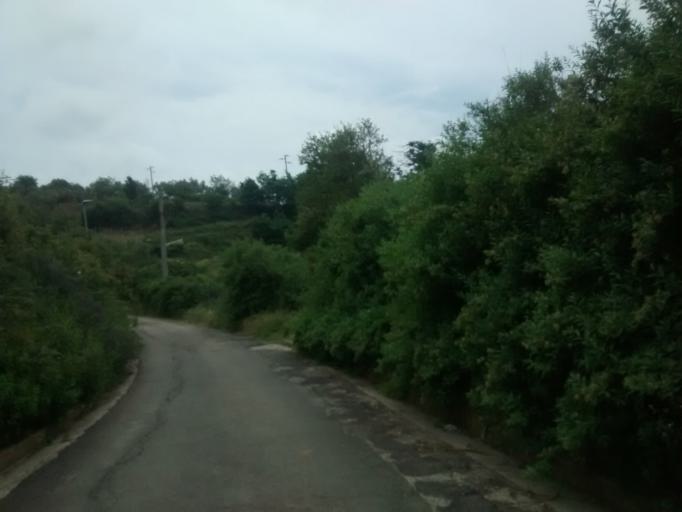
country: IT
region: Calabria
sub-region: Provincia di Catanzaro
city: Cortale
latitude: 38.8872
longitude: 16.4071
